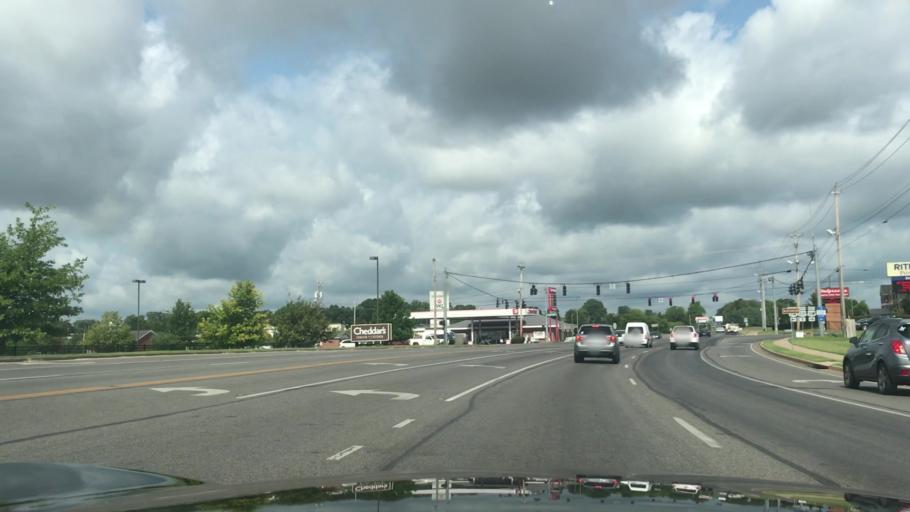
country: US
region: Kentucky
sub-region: Warren County
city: Bowling Green
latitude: 36.9619
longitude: -86.4667
